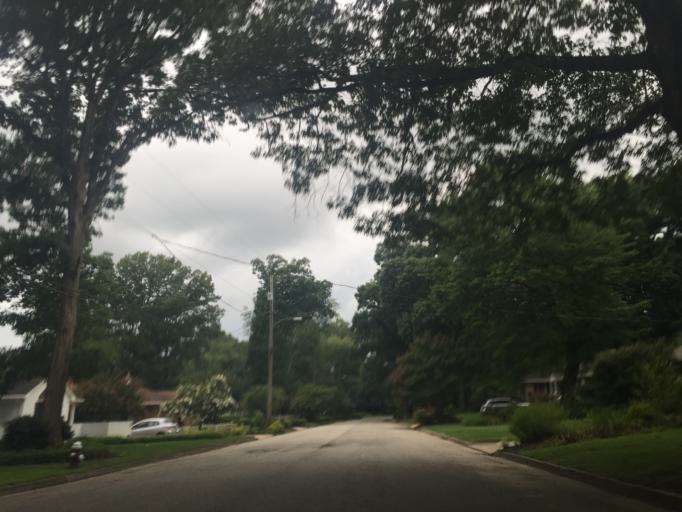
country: US
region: Virginia
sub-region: City of Newport News
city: Newport News
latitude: 37.0701
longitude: -76.5000
